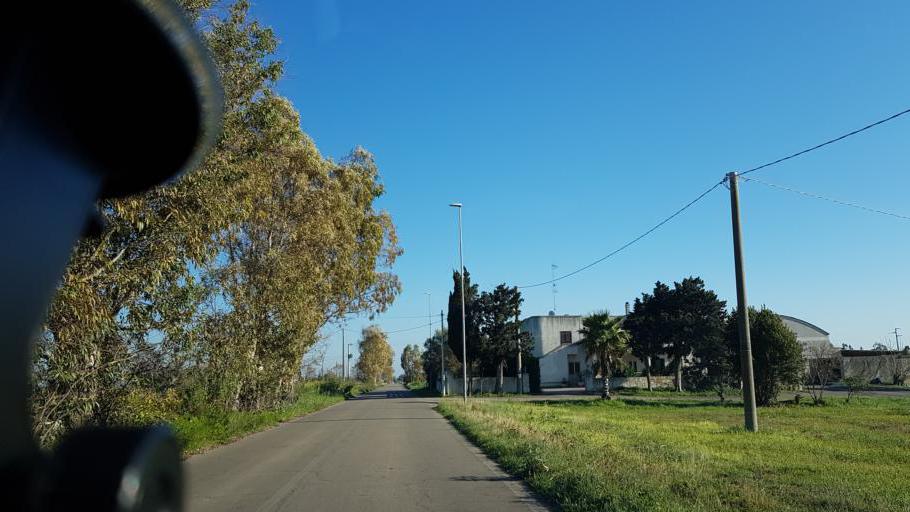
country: IT
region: Apulia
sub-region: Provincia di Lecce
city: Merine
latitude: 40.4220
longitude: 18.2475
